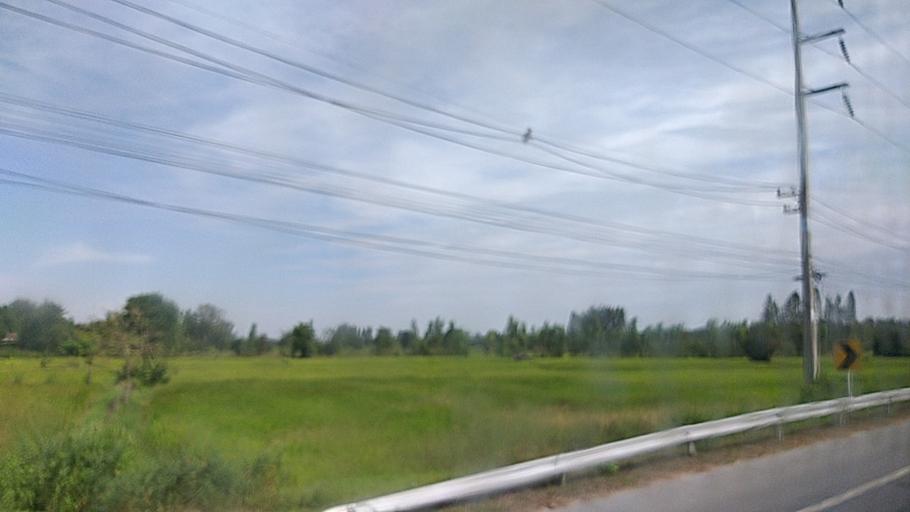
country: TH
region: Maha Sarakham
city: Chiang Yuen
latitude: 16.4462
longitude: 103.0353
